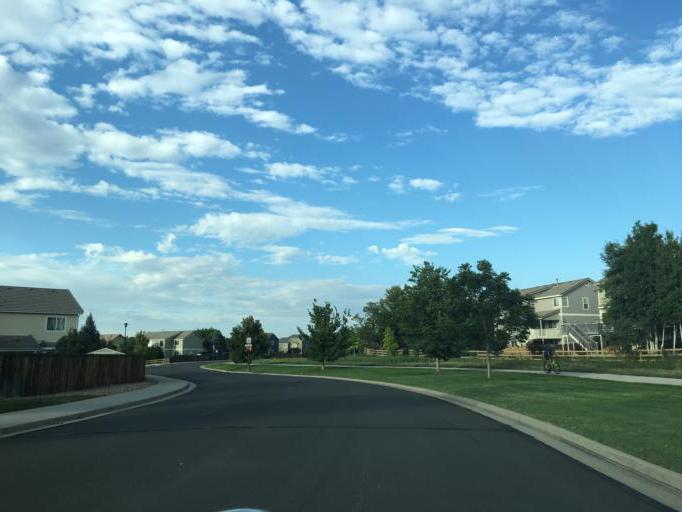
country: US
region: Colorado
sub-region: Adams County
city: Northglenn
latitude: 39.9447
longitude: -104.9539
